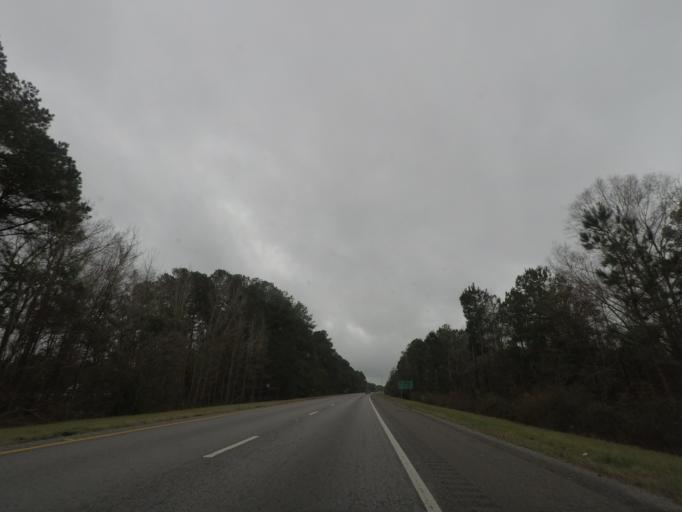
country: US
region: South Carolina
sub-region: Orangeburg County
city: Holly Hill
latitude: 33.4477
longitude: -80.4812
